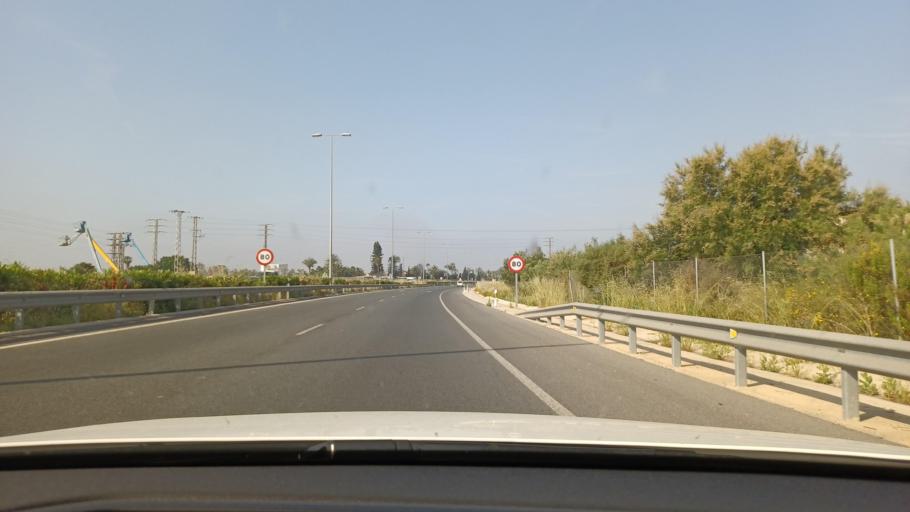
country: ES
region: Valencia
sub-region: Provincia de Alicante
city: Elche
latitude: 38.2518
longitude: -0.6930
